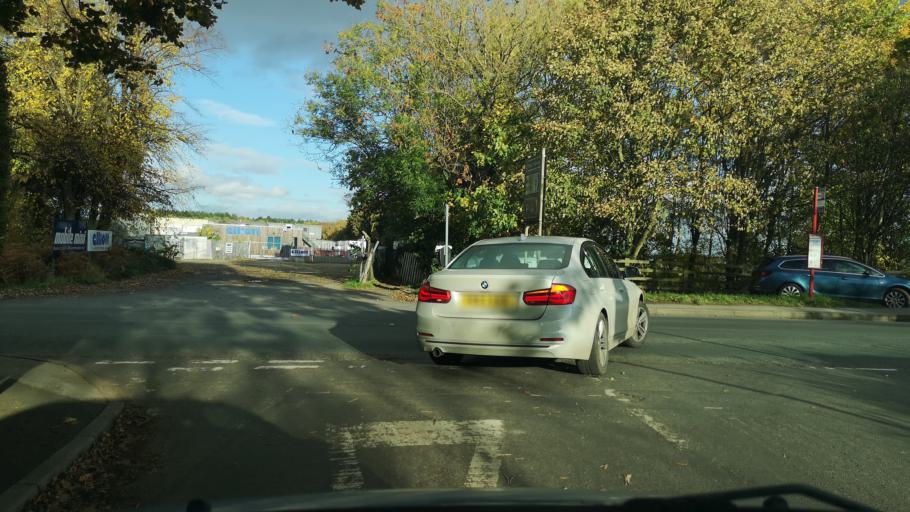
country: GB
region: England
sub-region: City and Borough of Wakefield
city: Woolley
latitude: 53.6219
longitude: -1.4992
